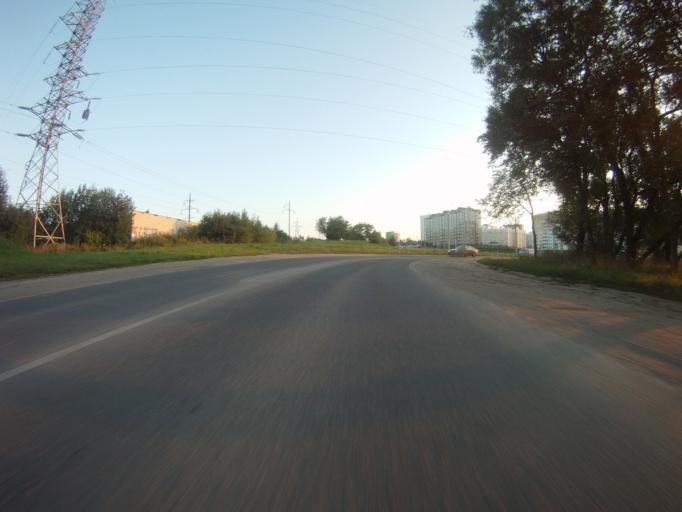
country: BY
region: Minsk
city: Novoye Medvezhino
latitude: 53.9195
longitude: 27.4683
